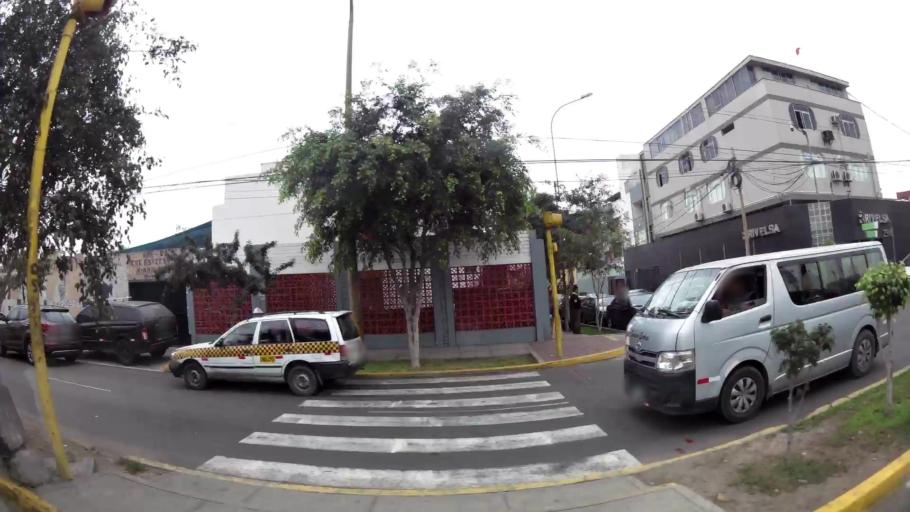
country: PE
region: Lima
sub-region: Lima
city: Surco
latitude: -12.1259
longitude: -77.0033
